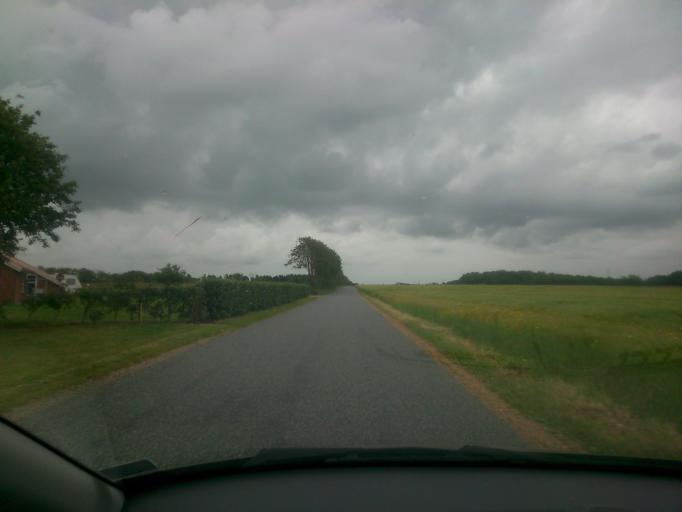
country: DK
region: South Denmark
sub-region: Esbjerg Kommune
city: Esbjerg
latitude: 55.5466
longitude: 8.4567
